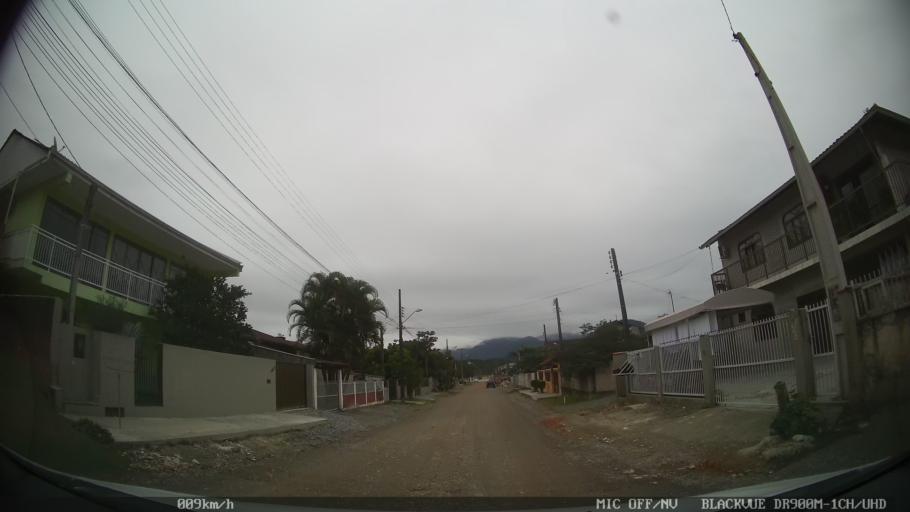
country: BR
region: Santa Catarina
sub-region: Joinville
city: Joinville
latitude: -26.2753
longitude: -48.9016
